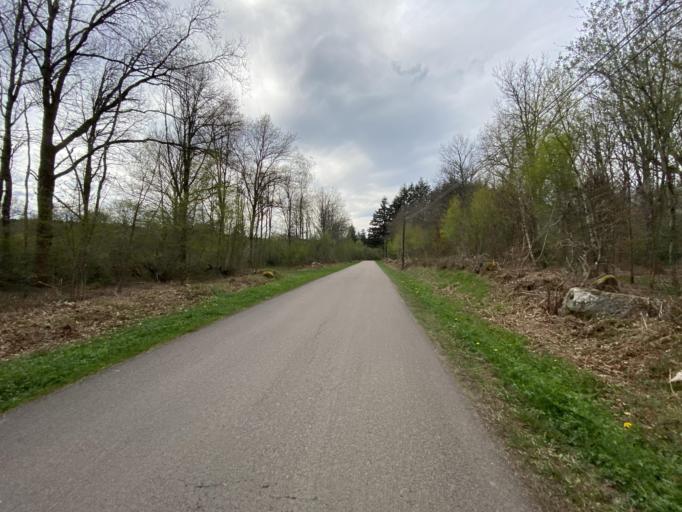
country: FR
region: Bourgogne
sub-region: Departement de la Cote-d'Or
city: Saulieu
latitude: 47.3194
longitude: 4.0673
